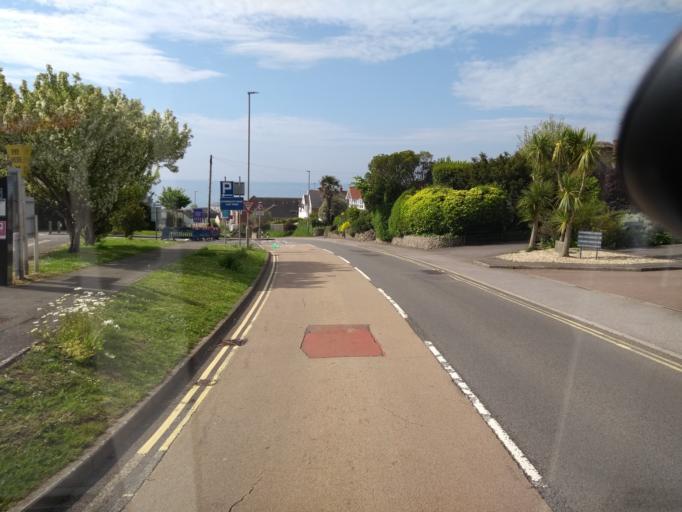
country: GB
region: England
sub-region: Dorset
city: Lyme Regis
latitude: 50.7292
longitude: -2.9316
